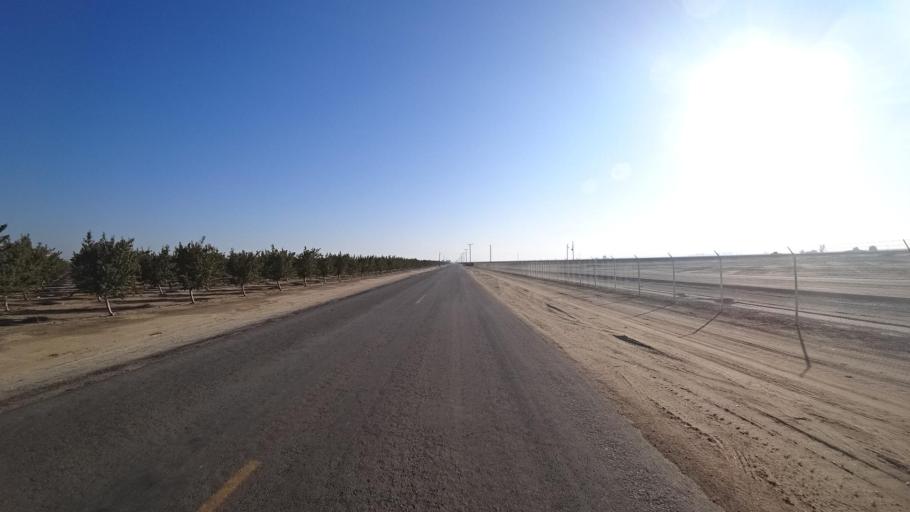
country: US
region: California
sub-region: Kern County
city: Delano
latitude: 35.7686
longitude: -119.2119
